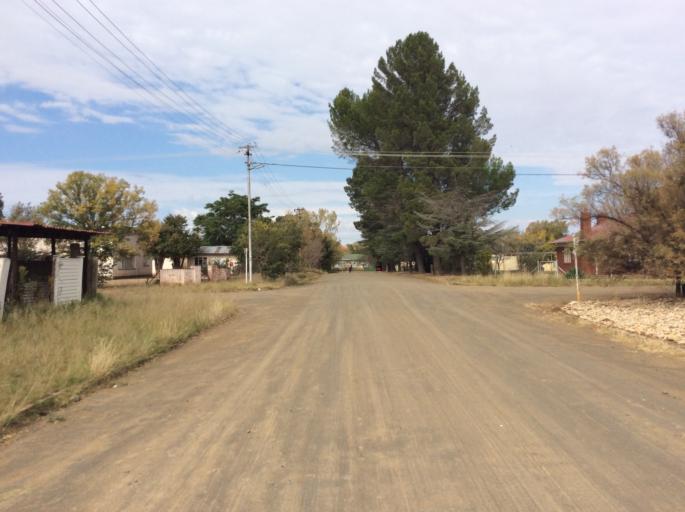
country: LS
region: Mafeteng
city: Mafeteng
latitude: -29.7299
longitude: 27.0302
